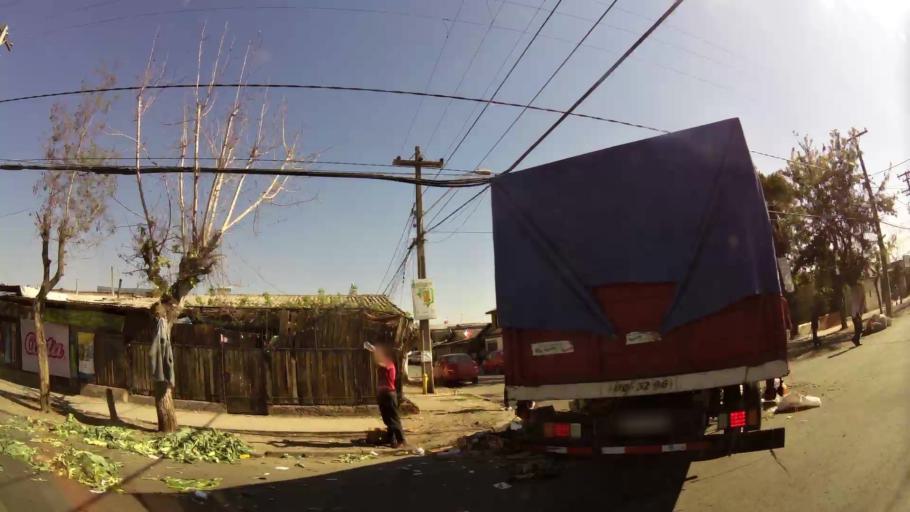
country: CL
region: Santiago Metropolitan
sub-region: Provincia de Santiago
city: Santiago
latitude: -33.5133
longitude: -70.6948
